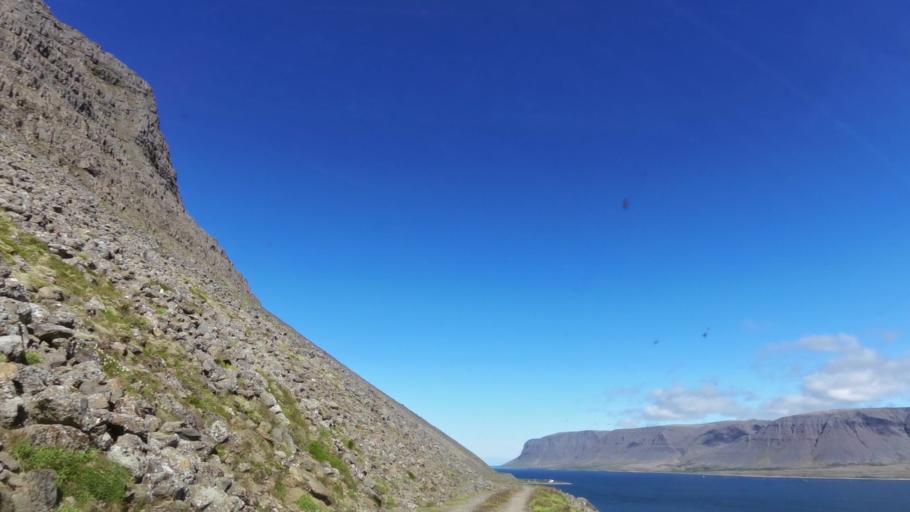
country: IS
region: West
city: Olafsvik
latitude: 65.6302
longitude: -23.9126
